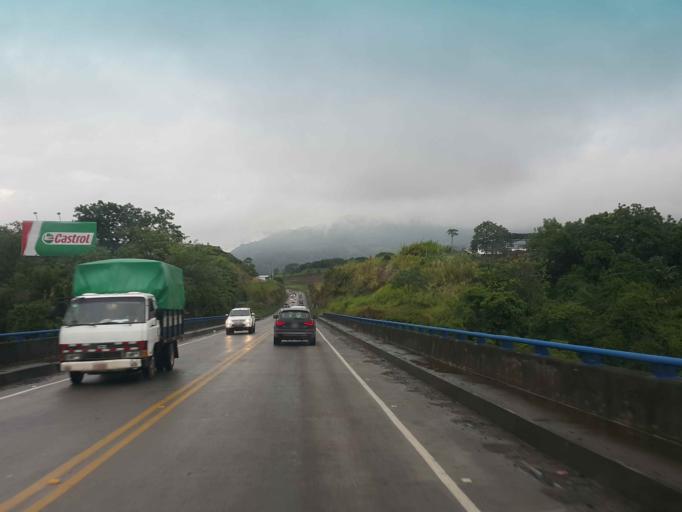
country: CR
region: Heredia
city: Colon
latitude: 9.9473
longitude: -84.2322
